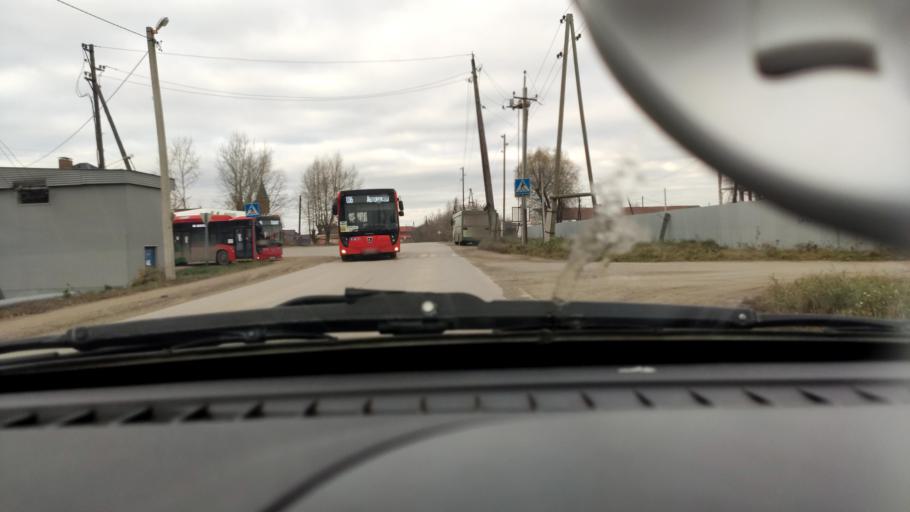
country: RU
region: Perm
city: Kondratovo
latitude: 57.9826
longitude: 56.1050
